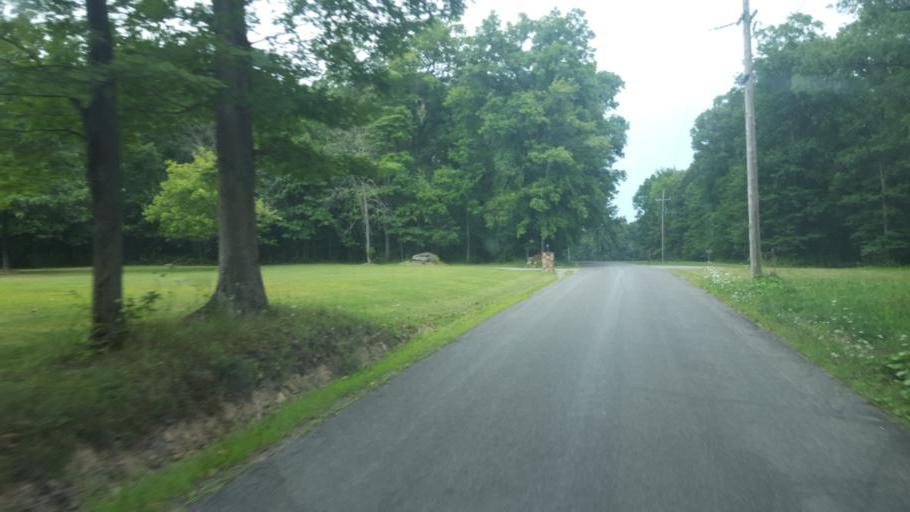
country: US
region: Pennsylvania
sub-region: Clarion County
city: Marianne
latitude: 41.2147
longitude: -79.4232
